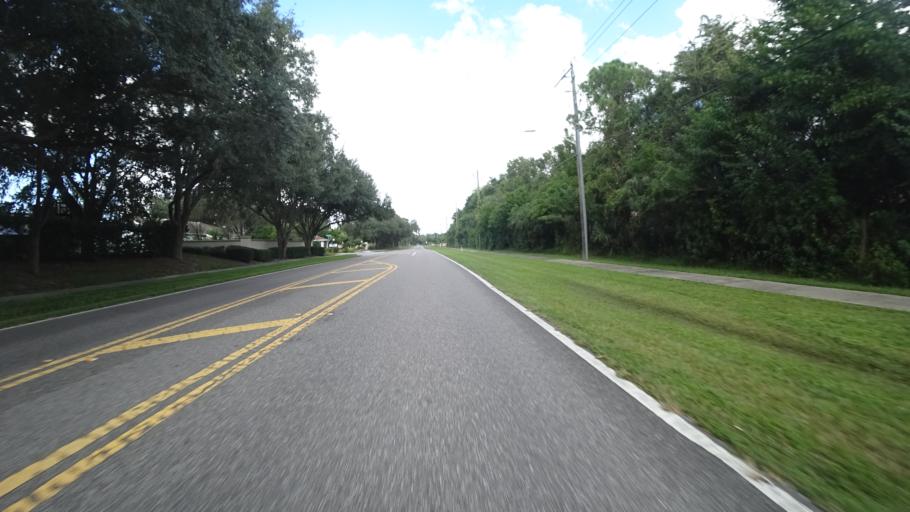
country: US
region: Florida
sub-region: Manatee County
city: Samoset
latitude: 27.4349
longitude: -82.5136
